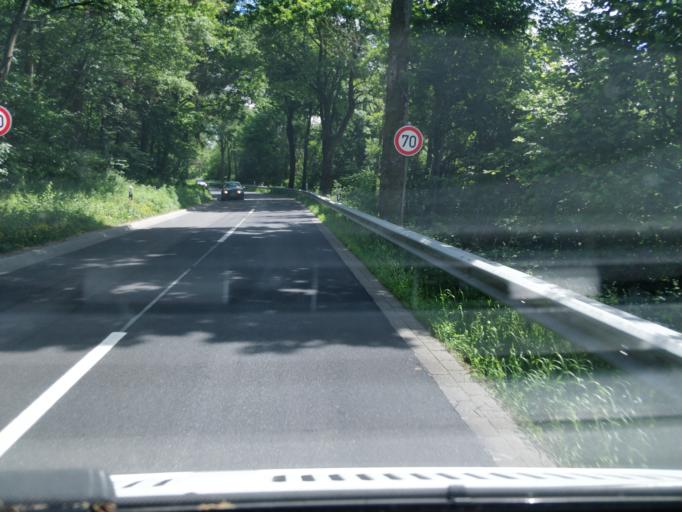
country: DE
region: Rheinland-Pfalz
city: Kerschenbach
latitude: 50.3606
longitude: 6.4693
